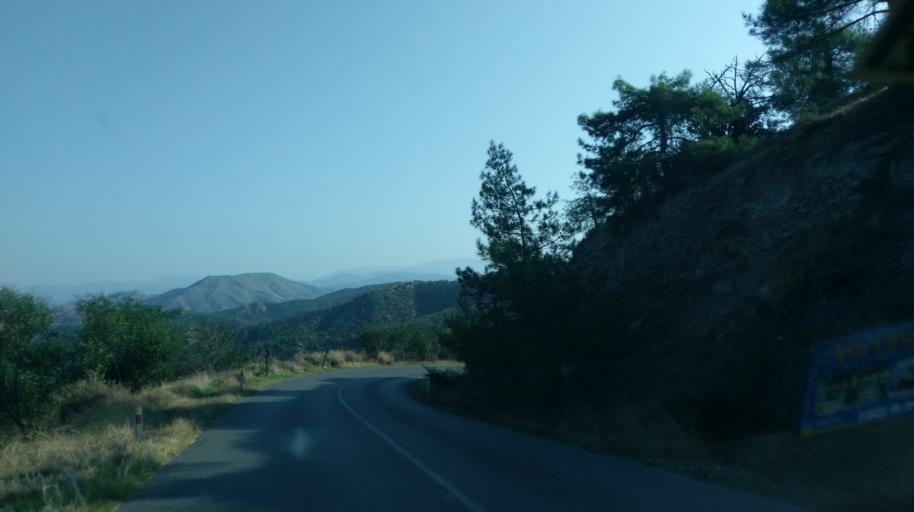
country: CY
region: Lefkosia
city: Kato Pyrgos
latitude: 35.1580
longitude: 32.7672
